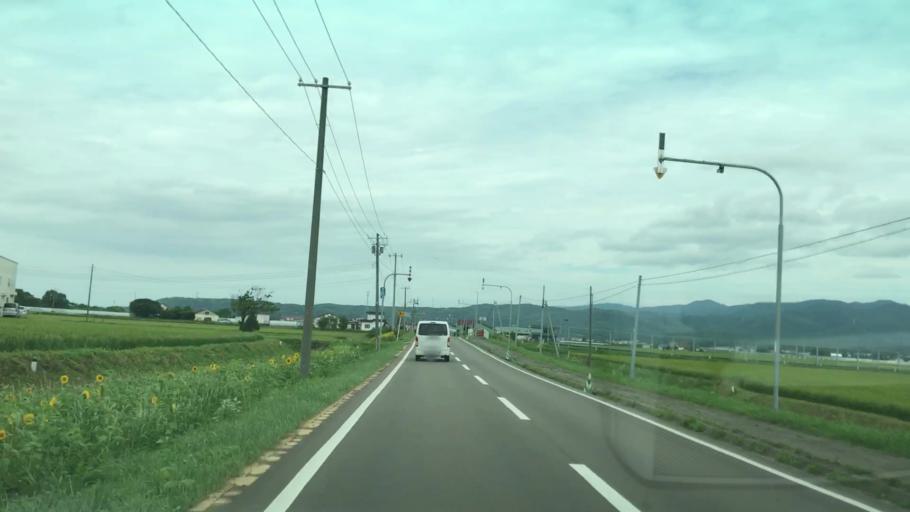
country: JP
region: Hokkaido
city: Iwanai
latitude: 43.0088
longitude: 140.5785
